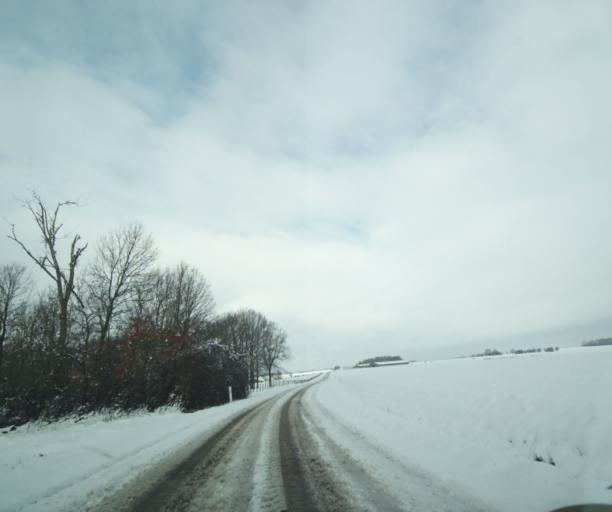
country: FR
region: Champagne-Ardenne
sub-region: Departement de la Haute-Marne
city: Montier-en-Der
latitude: 48.5156
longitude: 4.6813
